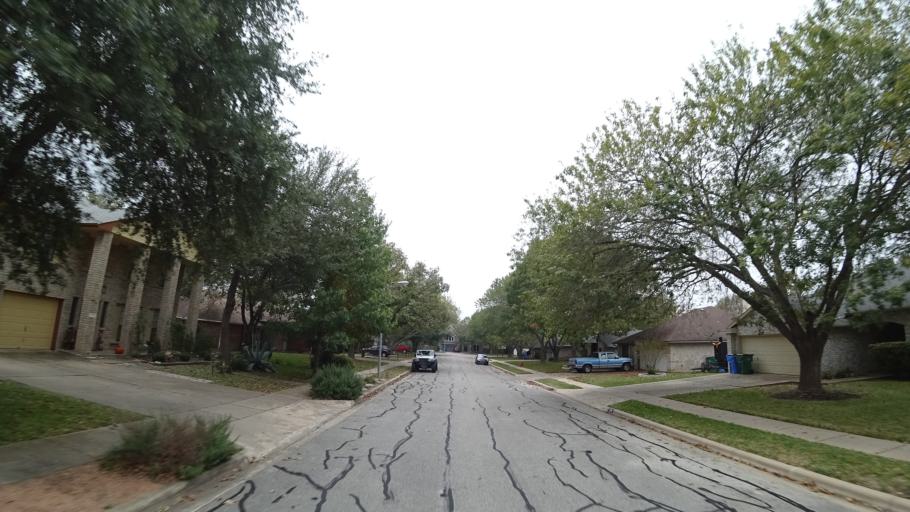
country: US
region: Texas
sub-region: Travis County
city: Pflugerville
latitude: 30.4490
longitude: -97.6109
